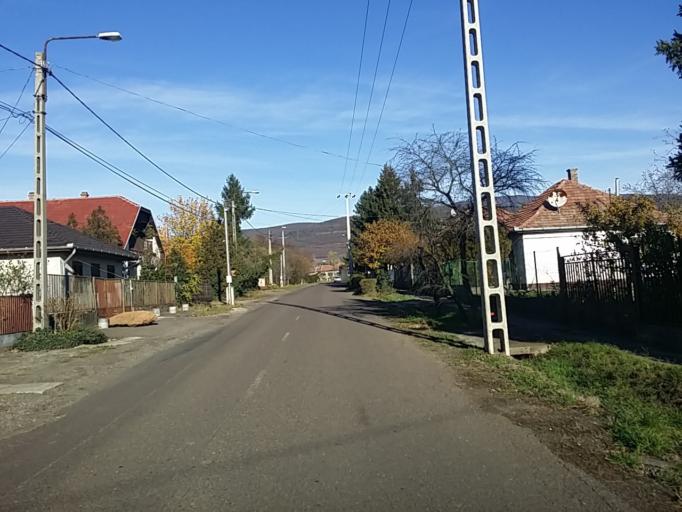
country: HU
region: Heves
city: Abasar
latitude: 47.8071
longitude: 20.0070
